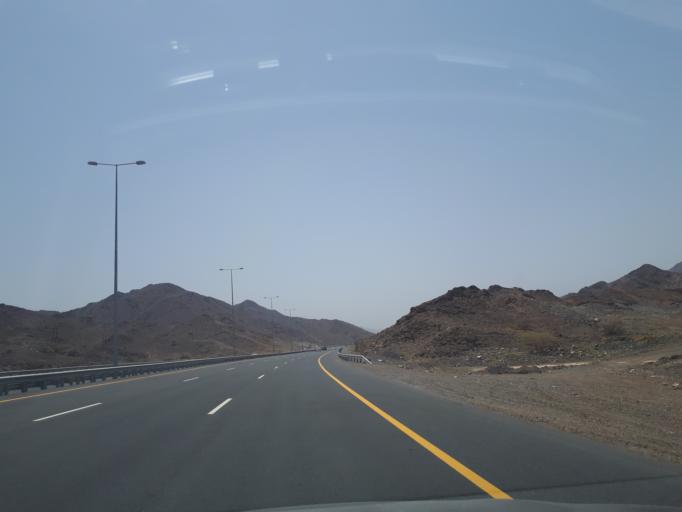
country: OM
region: Ash Sharqiyah
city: Ibra'
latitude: 22.8873
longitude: 58.2905
